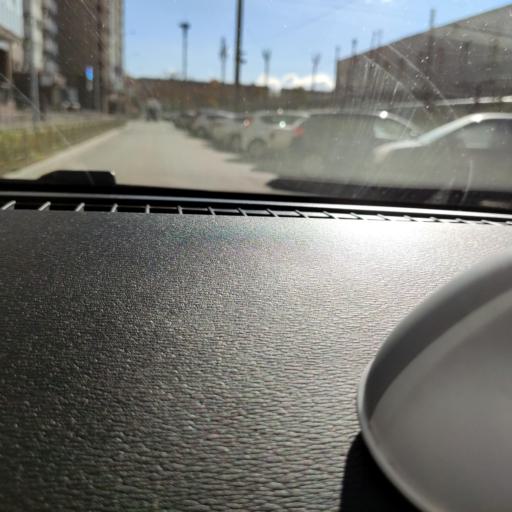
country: RU
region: Samara
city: Samara
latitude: 53.2165
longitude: 50.1913
